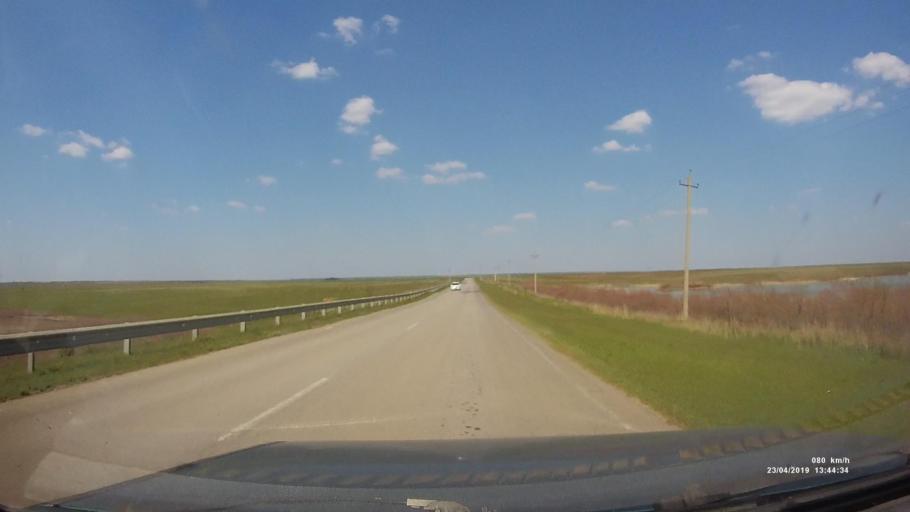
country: RU
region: Kalmykiya
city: Yashalta
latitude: 46.5808
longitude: 42.8176
